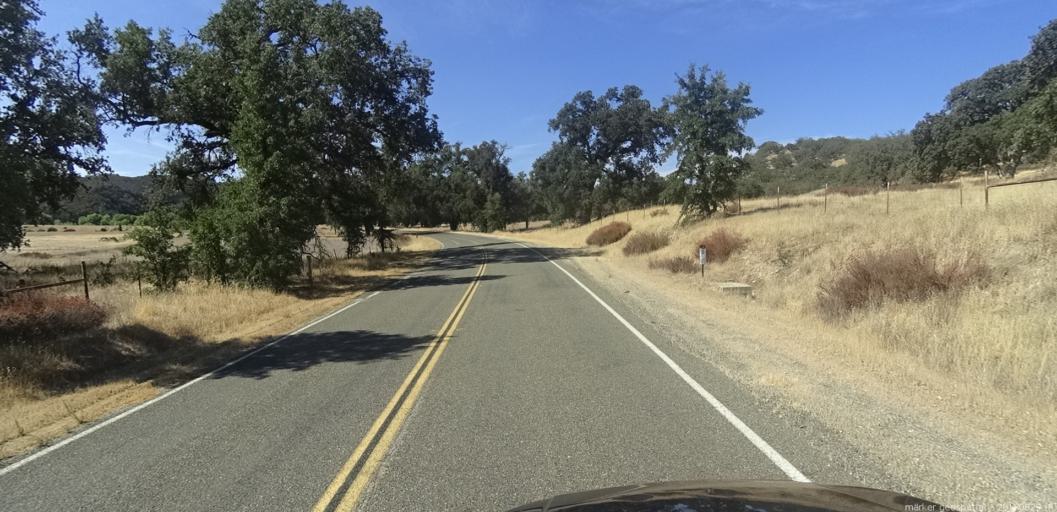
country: US
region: California
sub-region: San Luis Obispo County
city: Lake Nacimiento
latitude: 35.9010
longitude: -121.0900
